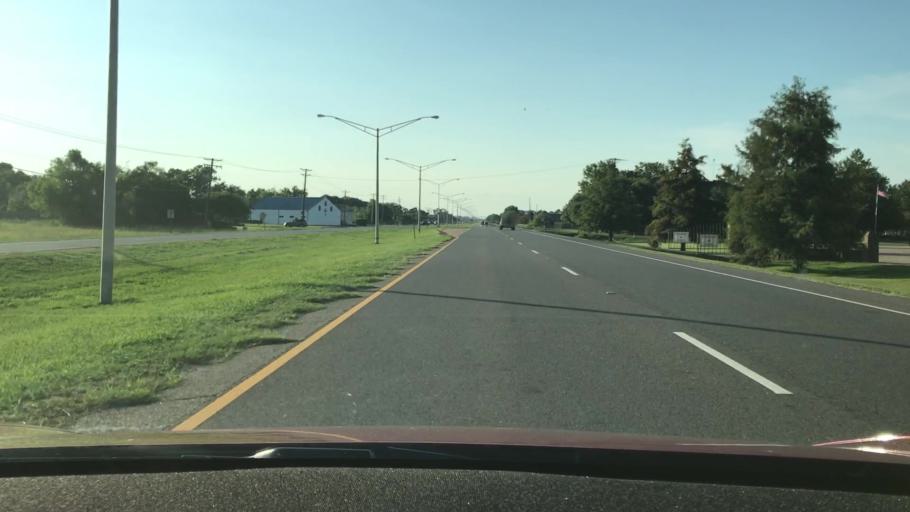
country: US
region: Louisiana
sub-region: Bossier Parish
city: Bossier City
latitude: 32.4069
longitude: -93.6974
